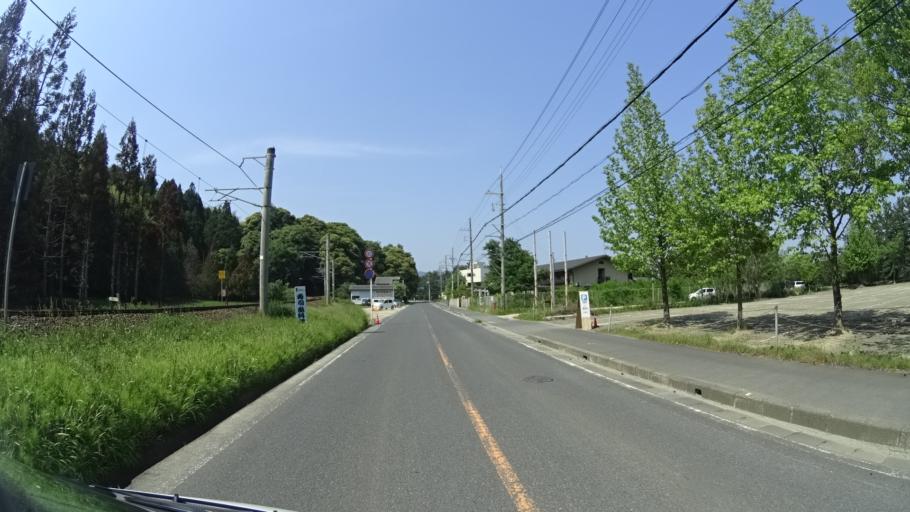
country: JP
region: Kyoto
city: Miyazu
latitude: 35.5527
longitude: 135.1867
